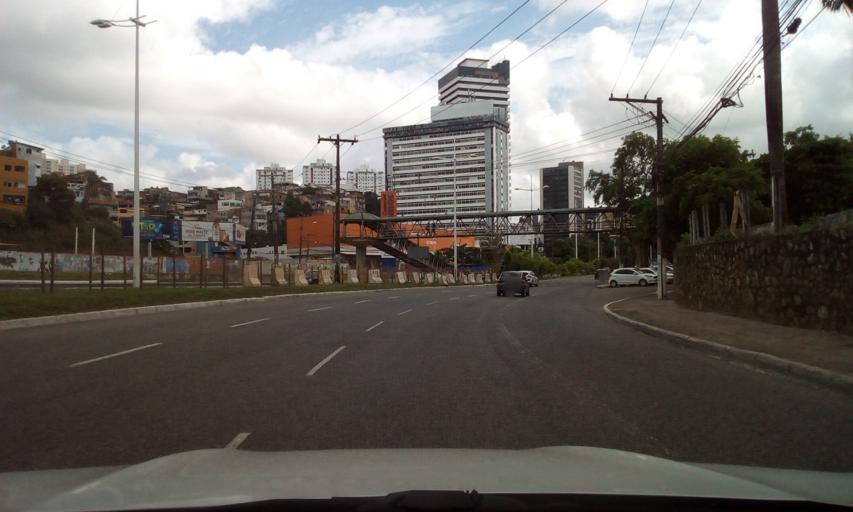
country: BR
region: Bahia
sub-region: Salvador
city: Salvador
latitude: -12.9925
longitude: -38.4753
